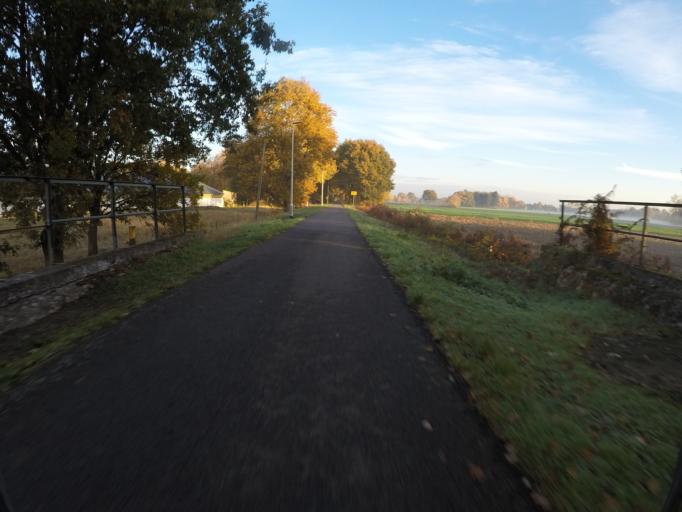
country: BE
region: Flanders
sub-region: Provincie Antwerpen
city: Hulshout
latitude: 51.1031
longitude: 4.8254
